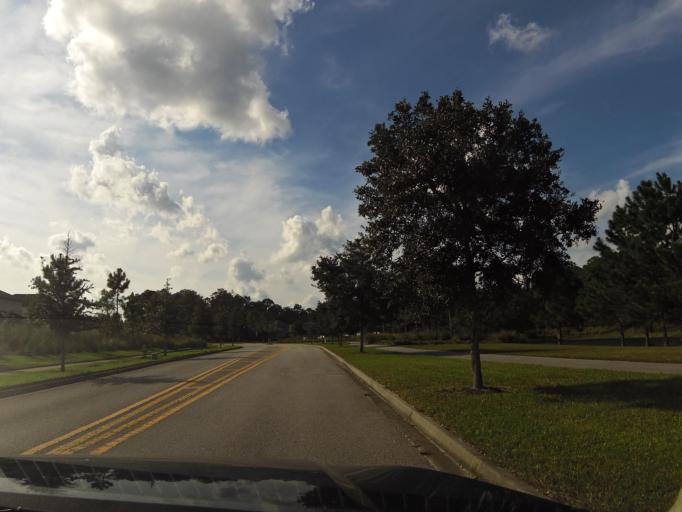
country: US
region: Florida
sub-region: Clay County
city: Green Cove Springs
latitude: 29.9317
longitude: -81.5149
